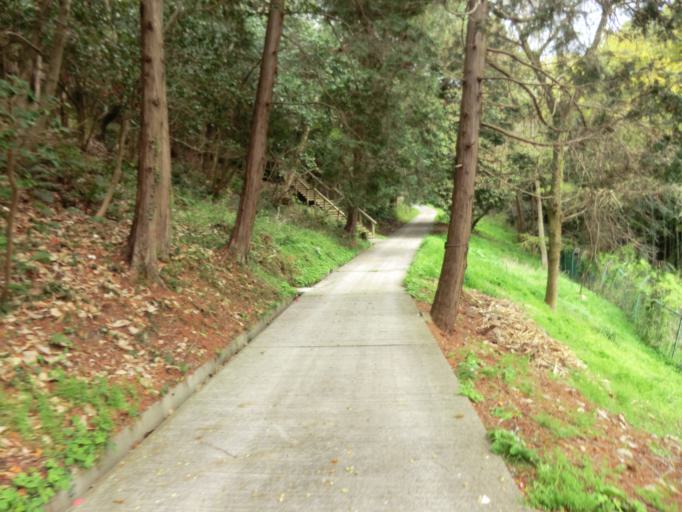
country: JP
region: Okayama
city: Okayama-shi
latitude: 34.6934
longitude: 133.9324
